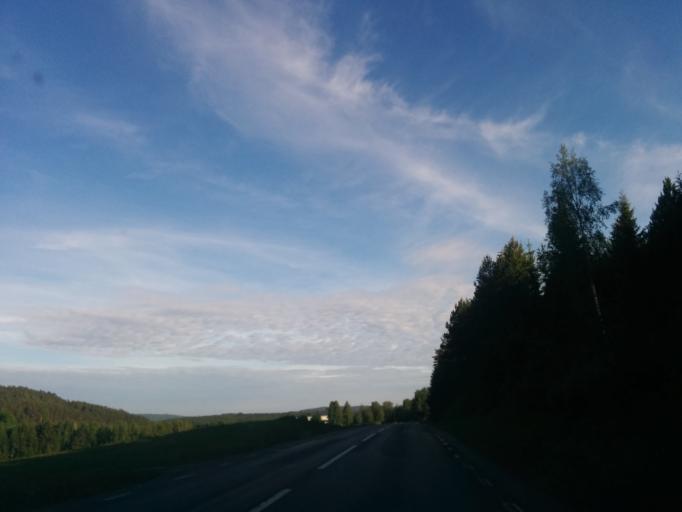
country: SE
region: Vaesternorrland
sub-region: Kramfors Kommun
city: Kramfors
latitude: 63.0073
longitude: 17.8332
